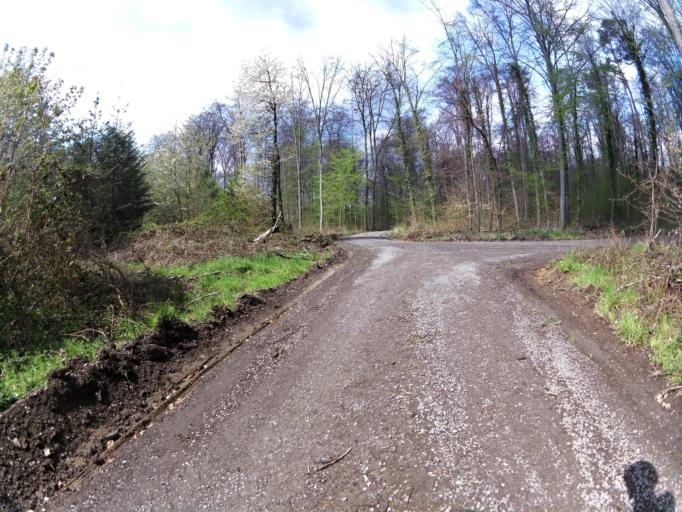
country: DE
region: Bavaria
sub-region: Regierungsbezirk Unterfranken
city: Waldbrunn
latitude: 49.7830
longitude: 9.7874
